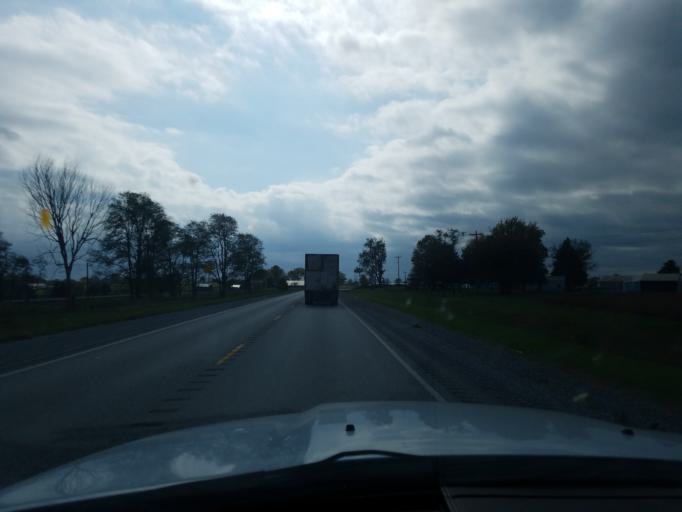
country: US
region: Kentucky
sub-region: Taylor County
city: Campbellsville
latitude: 37.3824
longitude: -85.2963
